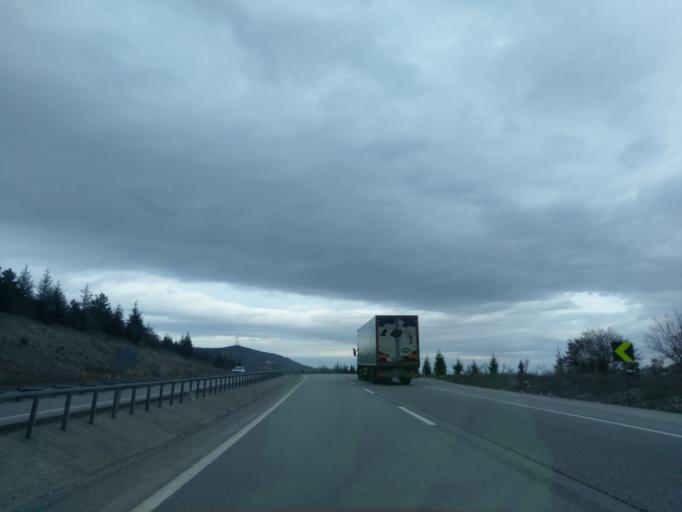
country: TR
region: Kuetahya
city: Sabuncu
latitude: 39.5951
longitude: 30.1428
